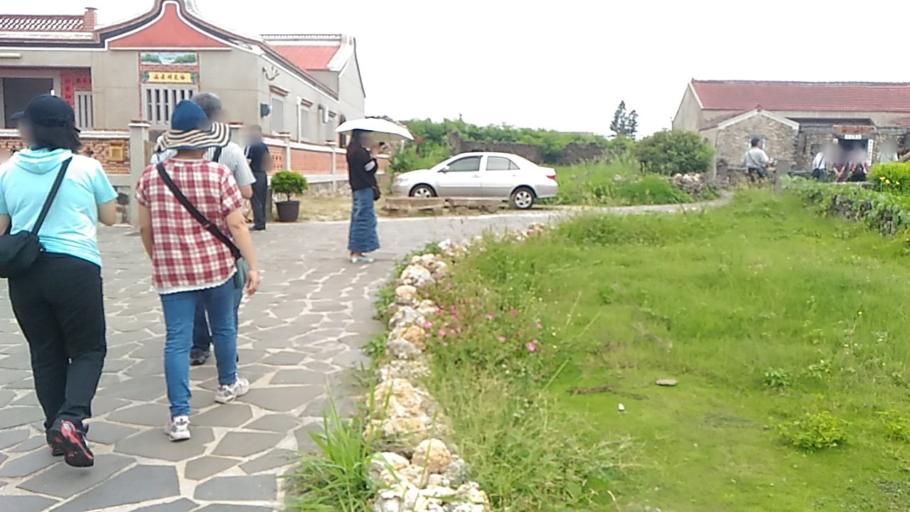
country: TW
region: Taiwan
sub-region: Penghu
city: Ma-kung
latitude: 23.6047
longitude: 119.5188
